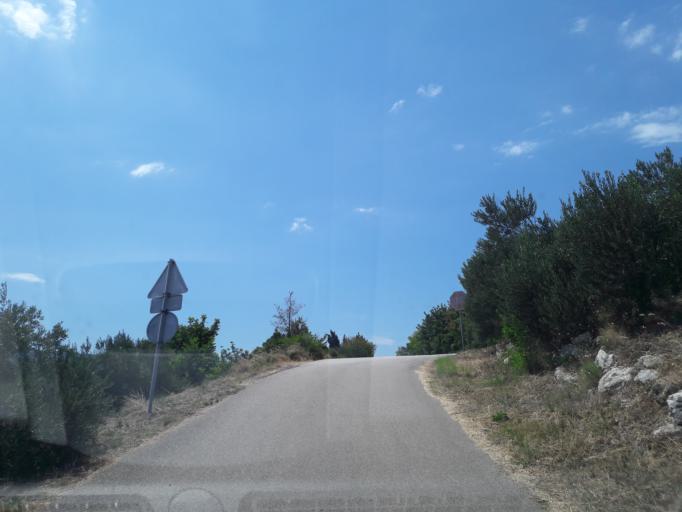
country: HR
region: Dubrovacko-Neretvanska
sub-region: Grad Korcula
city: Zrnovo
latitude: 42.9838
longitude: 17.0812
